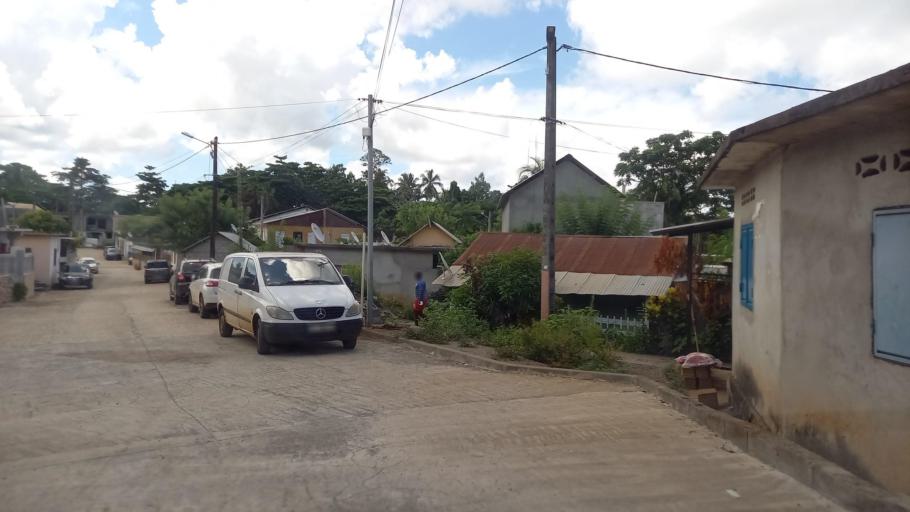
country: YT
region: Chirongui
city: Chirongui
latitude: -12.8922
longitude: 45.1404
